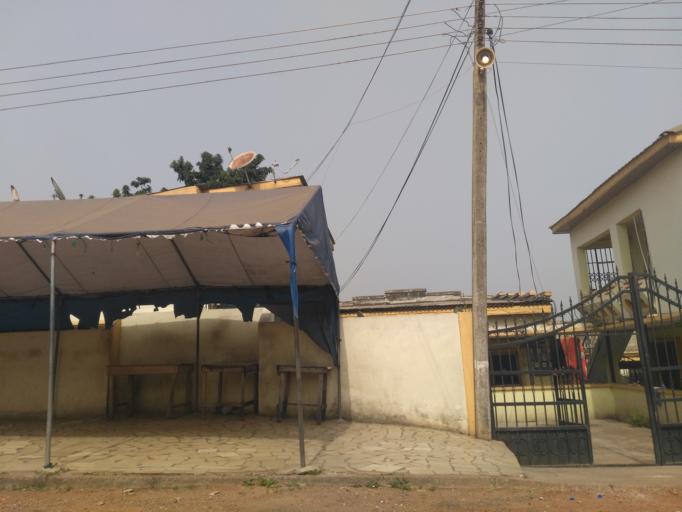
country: GH
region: Ashanti
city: Kumasi
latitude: 6.6746
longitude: -1.6023
